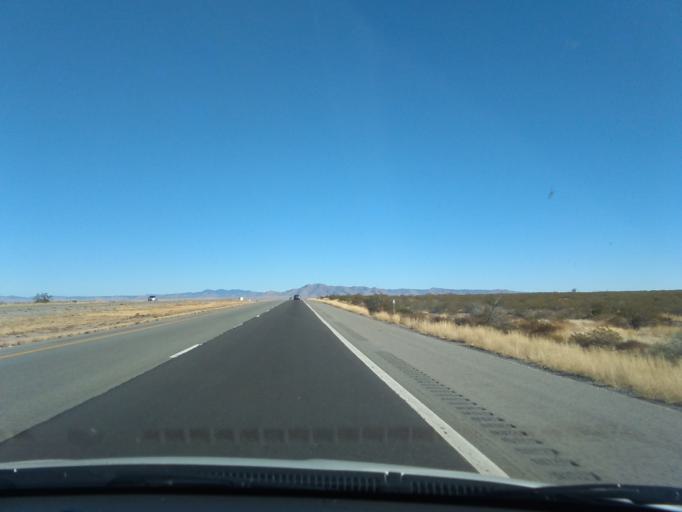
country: US
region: New Mexico
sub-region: Hidalgo County
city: Lordsburg
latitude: 32.3396
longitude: -108.7768
